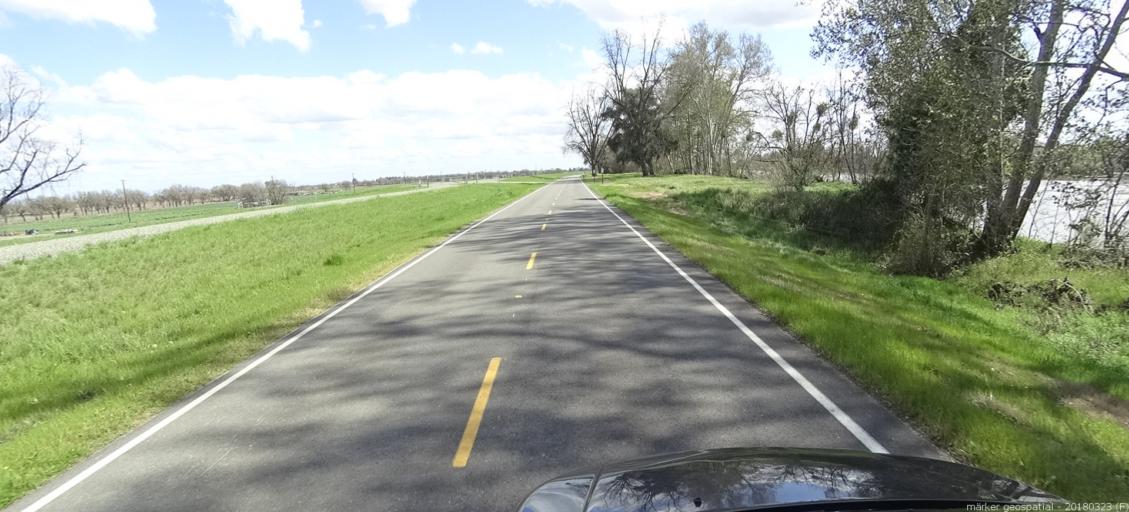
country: US
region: California
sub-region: Yolo County
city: West Sacramento
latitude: 38.6643
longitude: -121.6112
